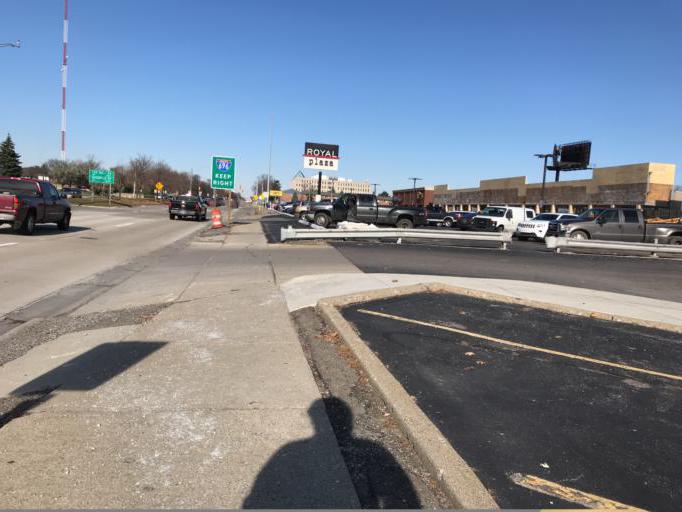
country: US
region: Michigan
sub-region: Oakland County
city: Southfield
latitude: 42.4751
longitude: -83.2016
